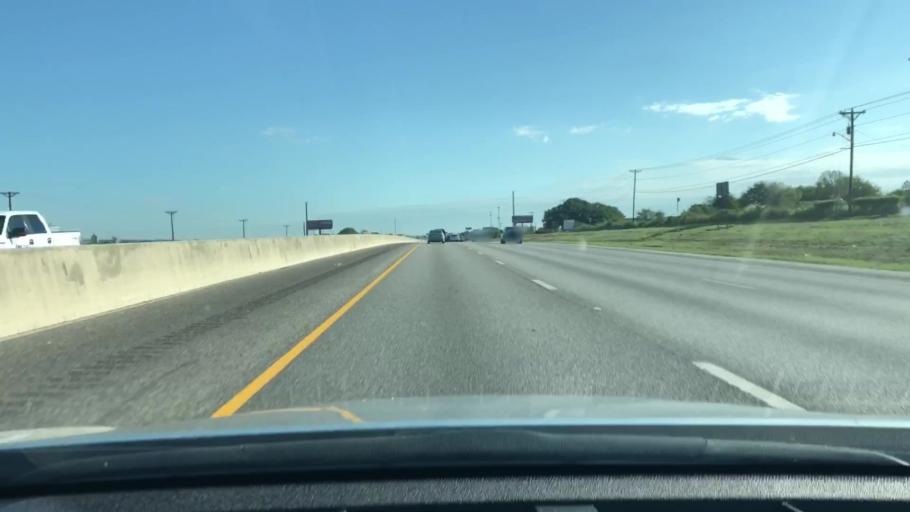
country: US
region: Texas
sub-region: Guadalupe County
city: Northcliff
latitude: 29.6442
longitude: -98.2042
